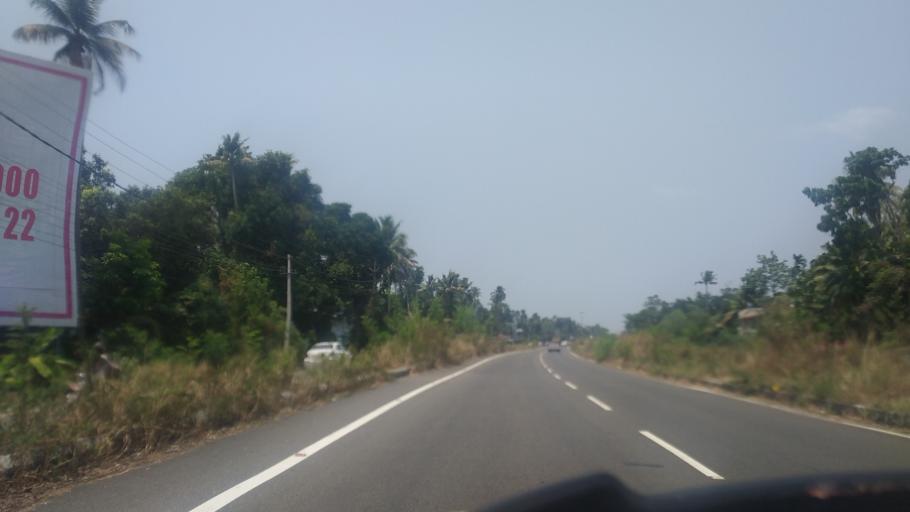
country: IN
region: Kerala
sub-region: Thrissur District
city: Kodungallur
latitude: 10.2183
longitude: 76.1962
